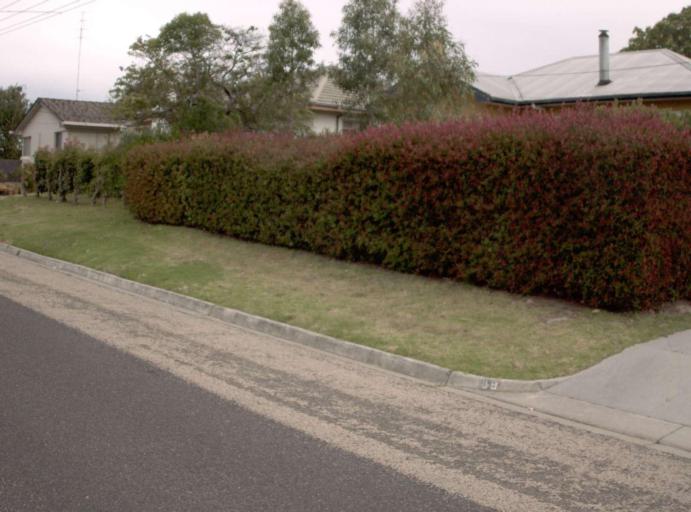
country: AU
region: Victoria
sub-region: East Gippsland
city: Bairnsdale
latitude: -37.9157
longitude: 147.7189
